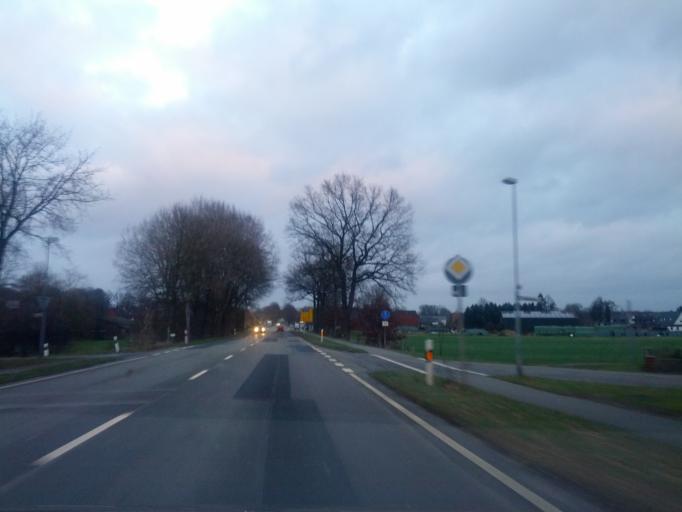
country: DE
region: Lower Saxony
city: Wistedt
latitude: 53.2686
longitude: 9.6775
